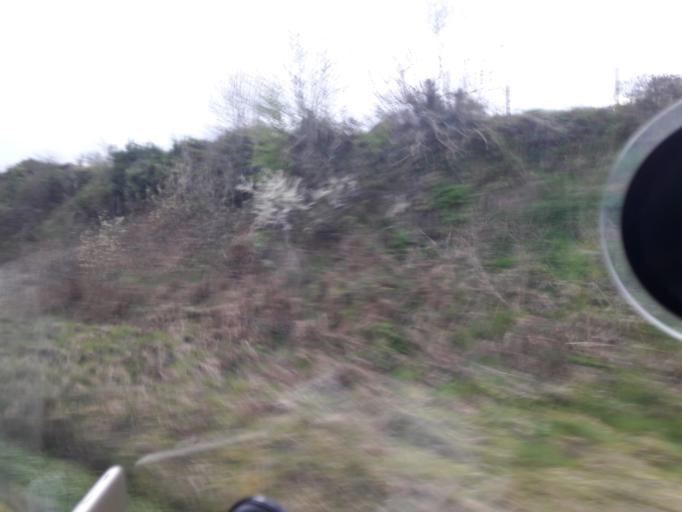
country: IE
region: Leinster
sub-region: An Iarmhi
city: An Muileann gCearr
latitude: 53.6316
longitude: -7.4179
